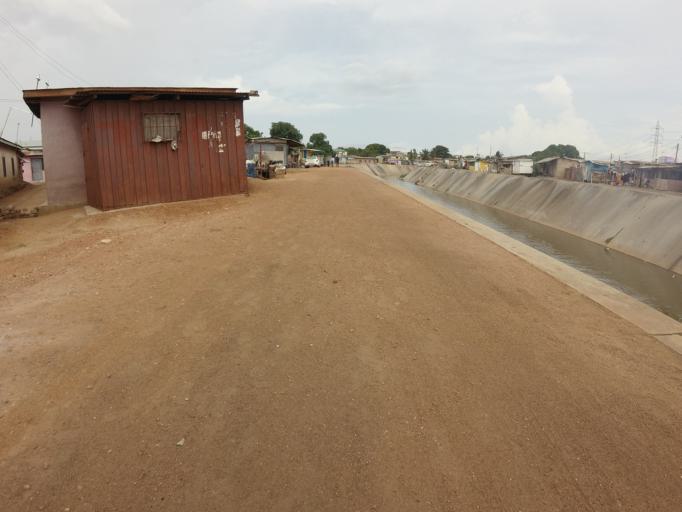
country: GH
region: Greater Accra
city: Accra
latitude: 5.5942
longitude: -0.2189
